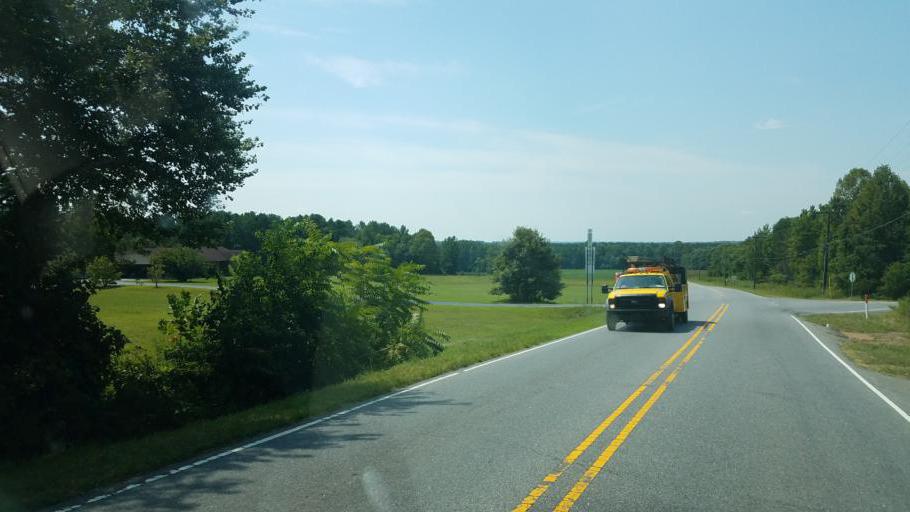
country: US
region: North Carolina
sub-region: Burke County
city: Icard
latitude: 35.5507
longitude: -81.5037
